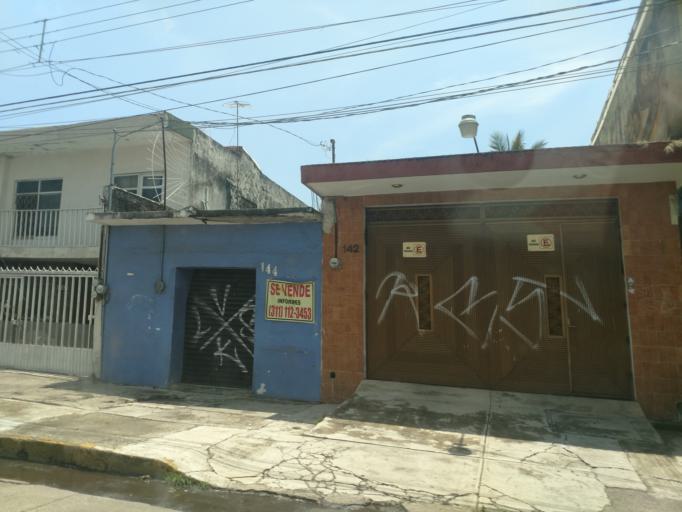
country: MX
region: Nayarit
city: Tepic
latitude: 21.5019
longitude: -104.8832
